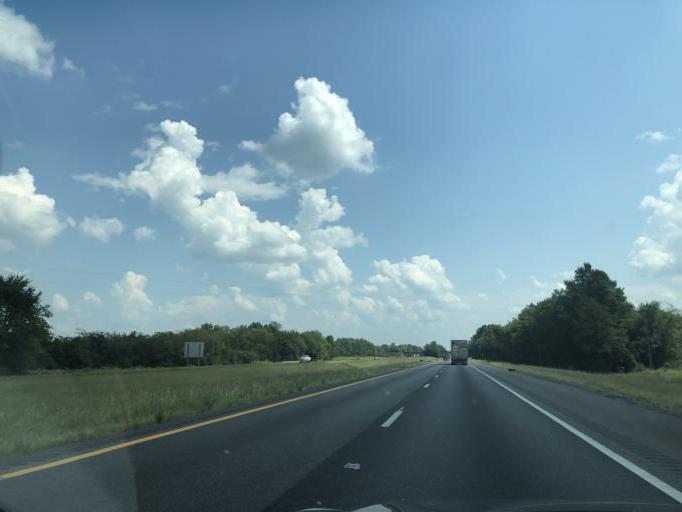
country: US
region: Tennessee
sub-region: Rutherford County
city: Plainview
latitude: 35.7686
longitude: -86.3603
